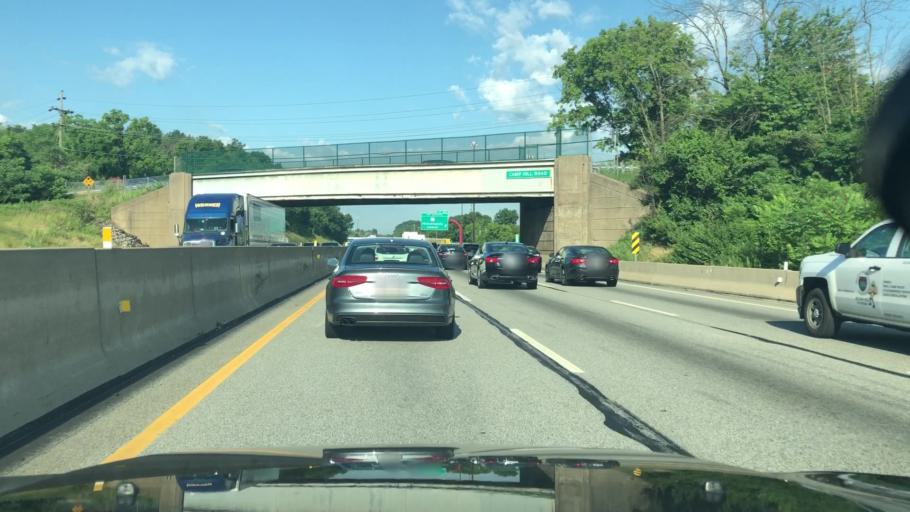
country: US
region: Pennsylvania
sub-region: Montgomery County
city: Oreland
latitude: 40.1346
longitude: -75.1855
